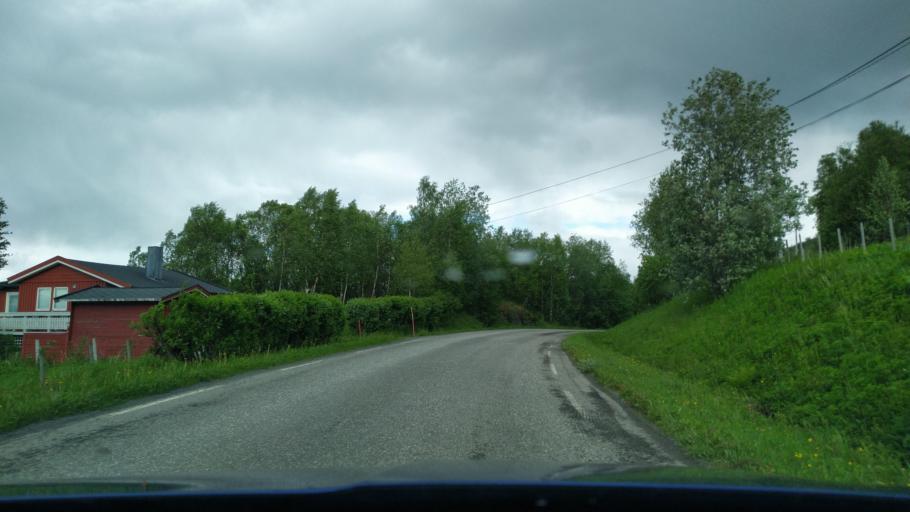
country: NO
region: Troms
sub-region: Lenvik
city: Finnsnes
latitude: 69.1360
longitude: 17.8995
